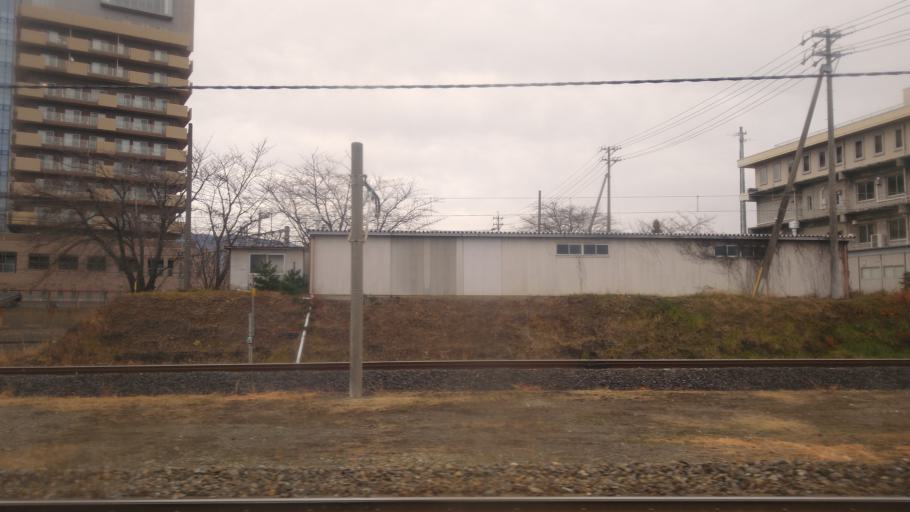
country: JP
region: Nagano
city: Shiojiri
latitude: 36.1131
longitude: 137.9473
